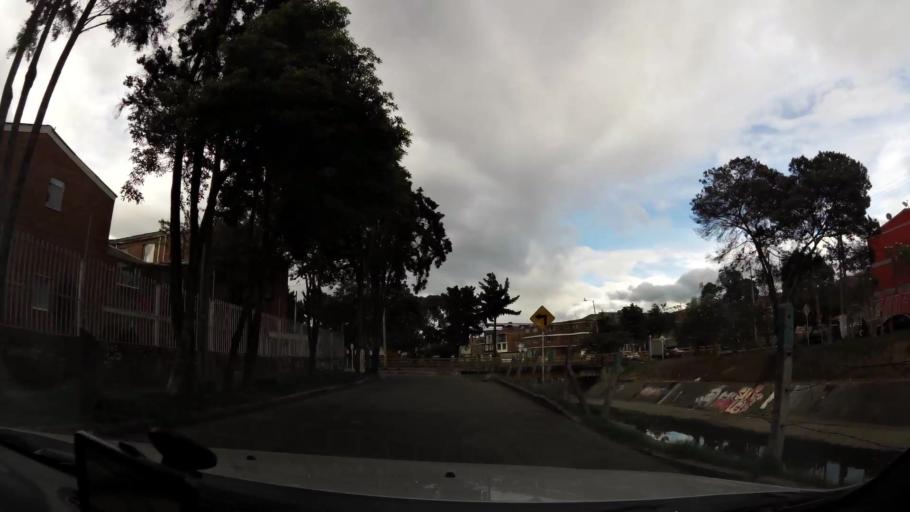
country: CO
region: Bogota D.C.
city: Bogota
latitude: 4.6070
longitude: -74.1200
